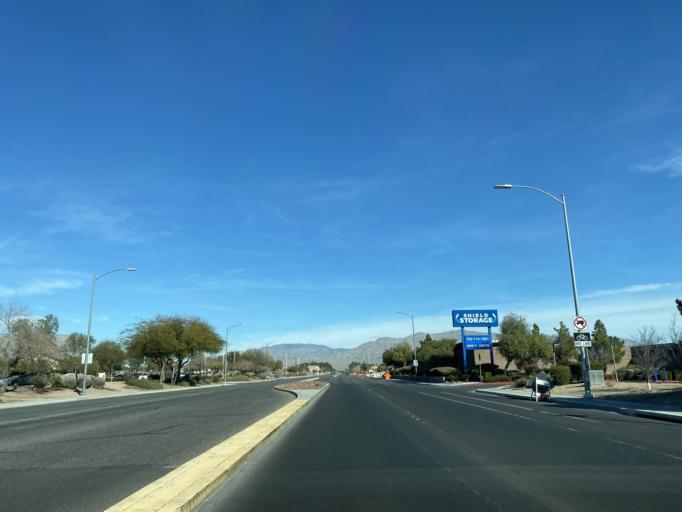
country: US
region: Nevada
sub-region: Clark County
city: Las Vegas
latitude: 36.2469
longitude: -115.2255
